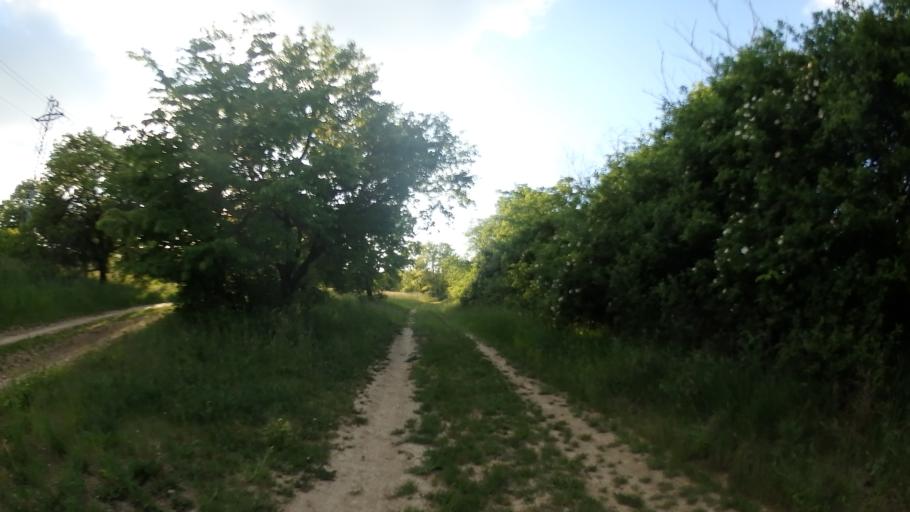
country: CZ
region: South Moravian
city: Zelesice
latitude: 49.1265
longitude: 16.5891
